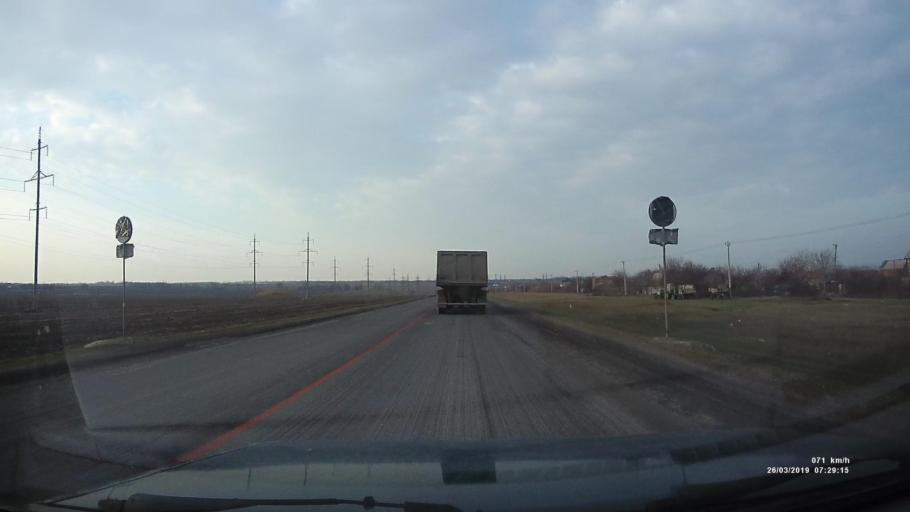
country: RU
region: Rostov
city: Novobessergenovka
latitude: 47.2470
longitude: 38.8181
